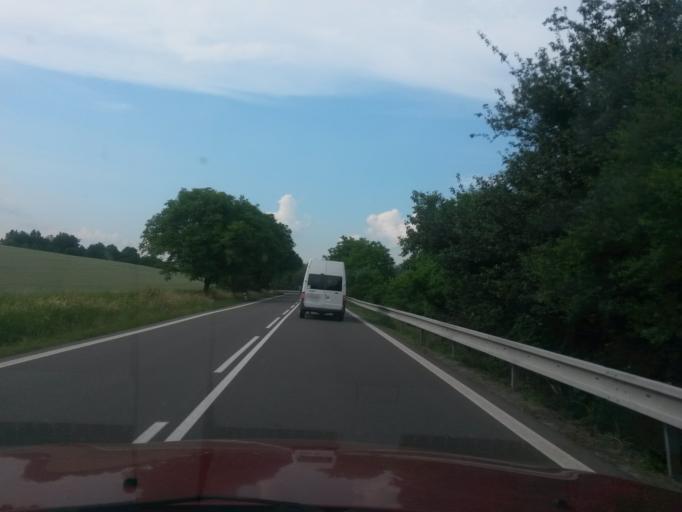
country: SK
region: Presovsky
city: Vranov nad Topl'ou
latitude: 48.9646
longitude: 21.5813
